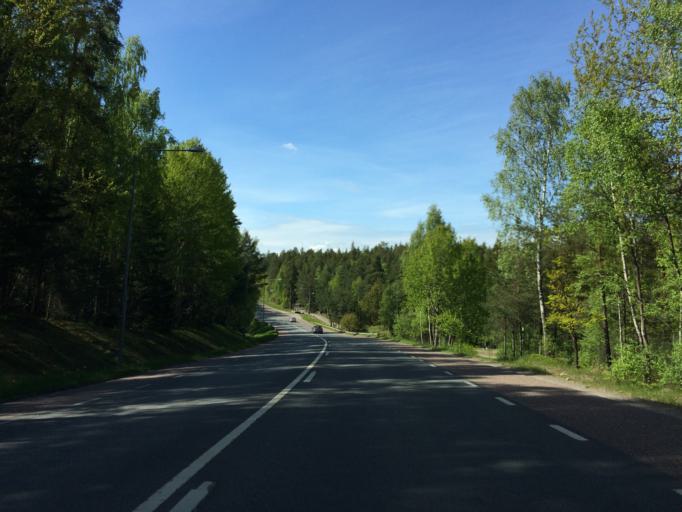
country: SE
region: Stockholm
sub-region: Sollentuna Kommun
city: Sollentuna
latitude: 59.4363
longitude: 17.9909
